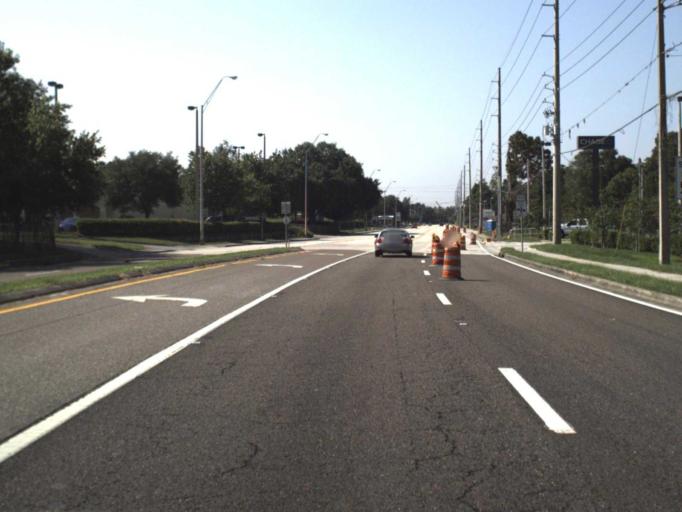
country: US
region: Florida
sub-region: Hillsborough County
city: Lake Magdalene
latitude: 28.1080
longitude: -82.4604
